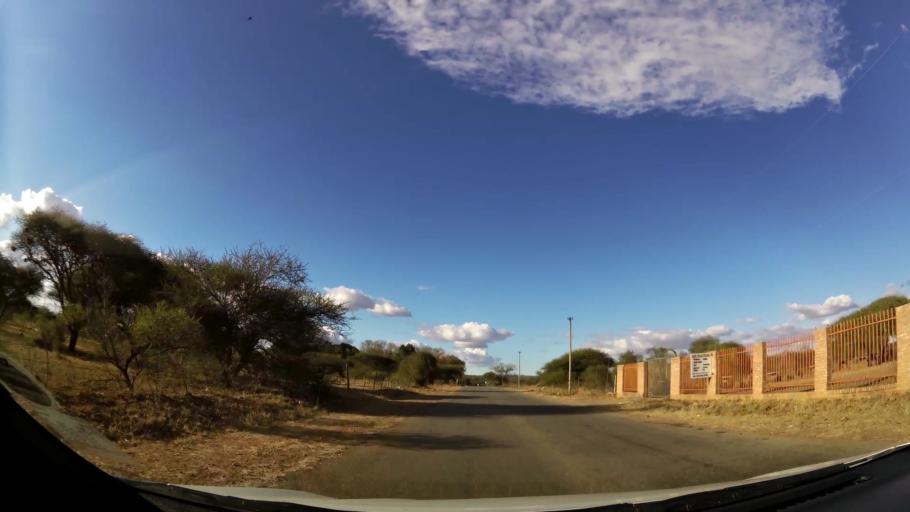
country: ZA
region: Limpopo
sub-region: Capricorn District Municipality
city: Polokwane
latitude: -23.9321
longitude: 29.4382
